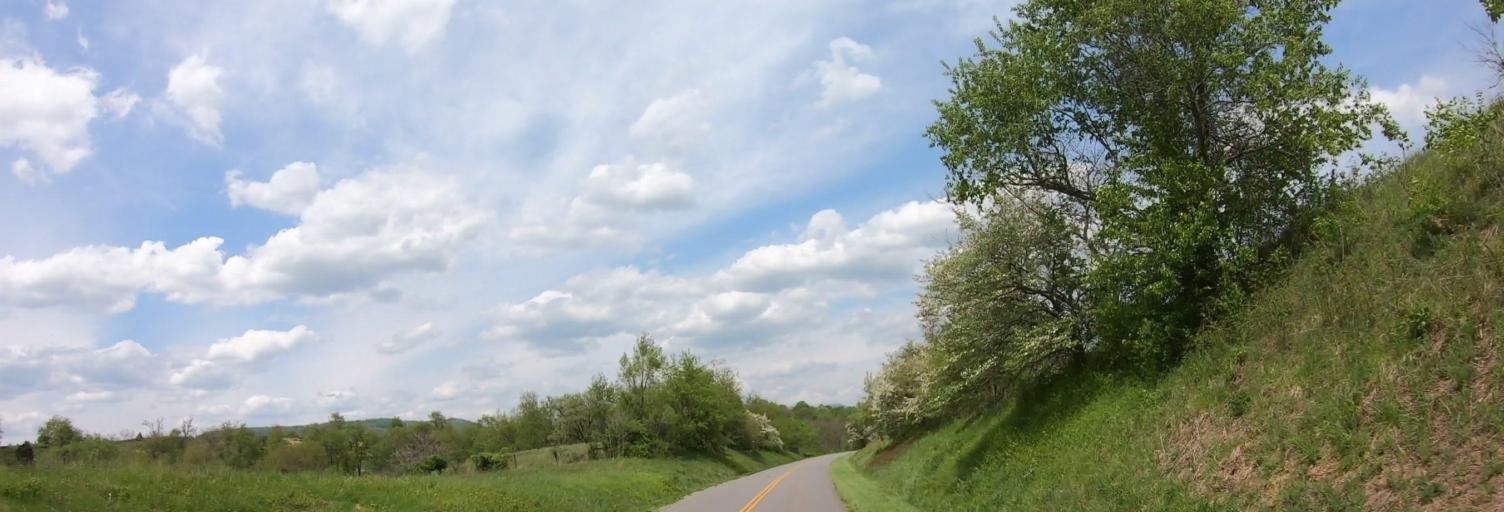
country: US
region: Virginia
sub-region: Botetourt County
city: Laymantown
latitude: 37.3273
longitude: -79.8572
